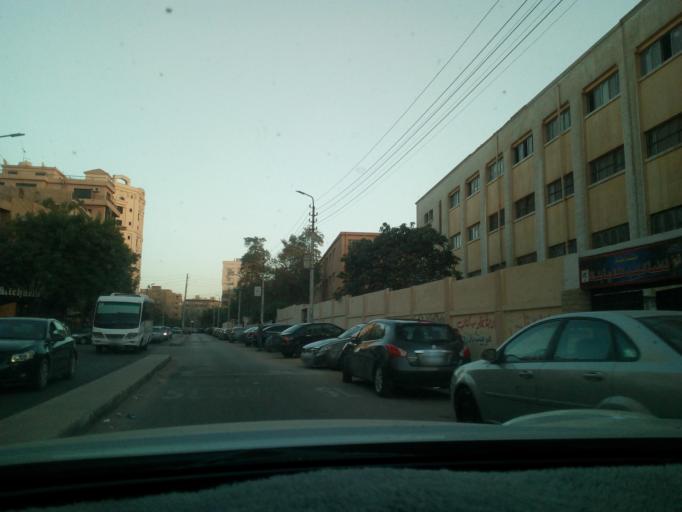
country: EG
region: Muhafazat al Qahirah
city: Cairo
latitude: 30.0911
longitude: 31.3436
